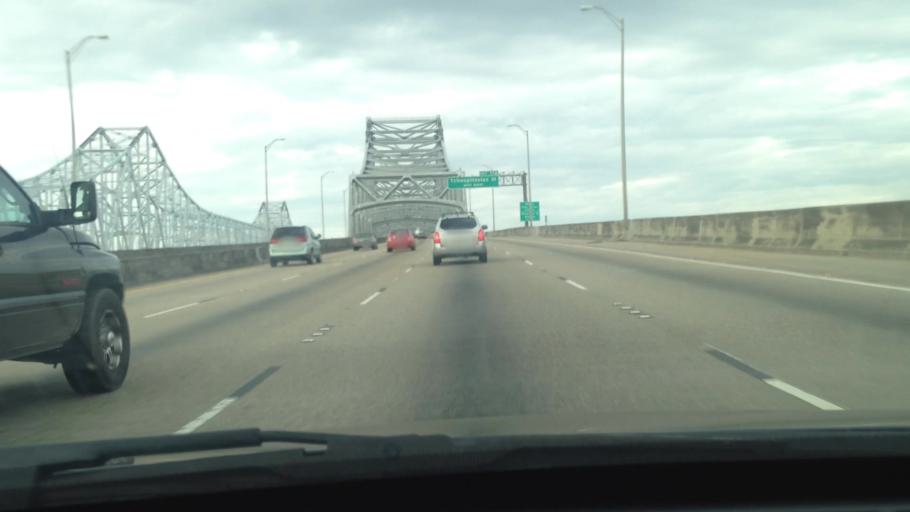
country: US
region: Louisiana
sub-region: Jefferson Parish
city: Gretna
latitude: 29.9389
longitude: -90.0496
